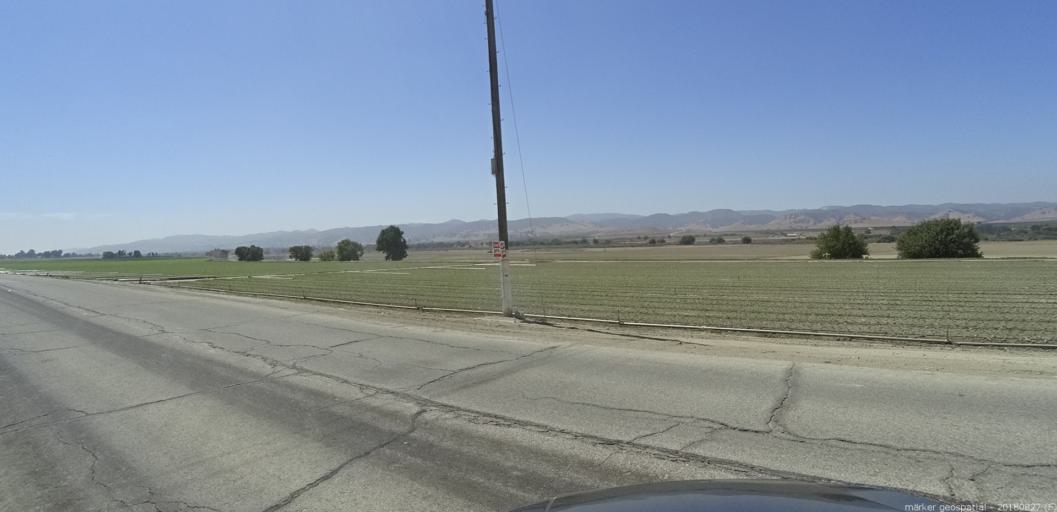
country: US
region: California
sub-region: Monterey County
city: King City
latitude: 36.0460
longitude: -120.9163
